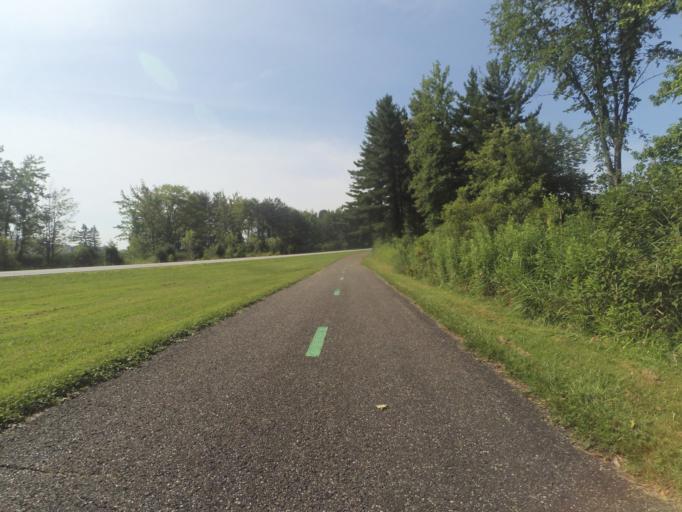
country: US
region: Ohio
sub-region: Cuyahoga County
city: Solon
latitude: 41.4088
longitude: -81.4729
